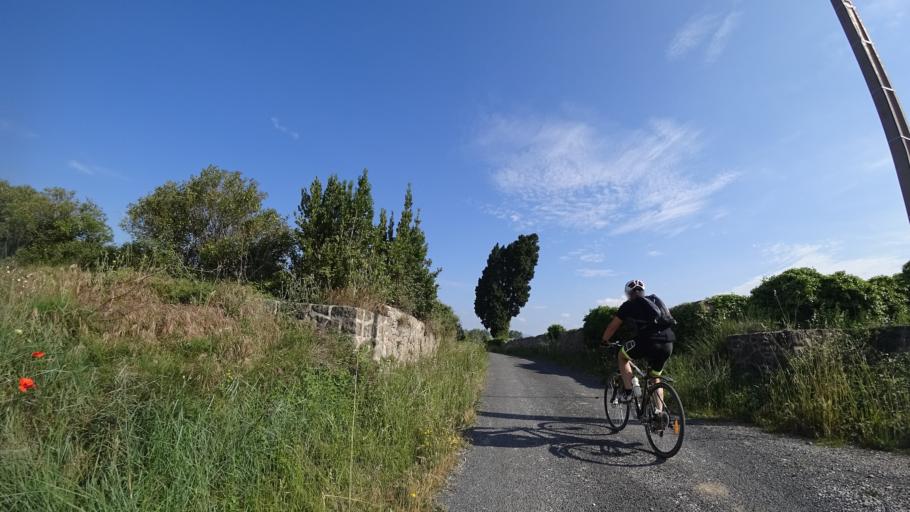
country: FR
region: Languedoc-Roussillon
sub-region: Departement de l'Herault
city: Olonzac
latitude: 43.2634
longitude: 2.7213
